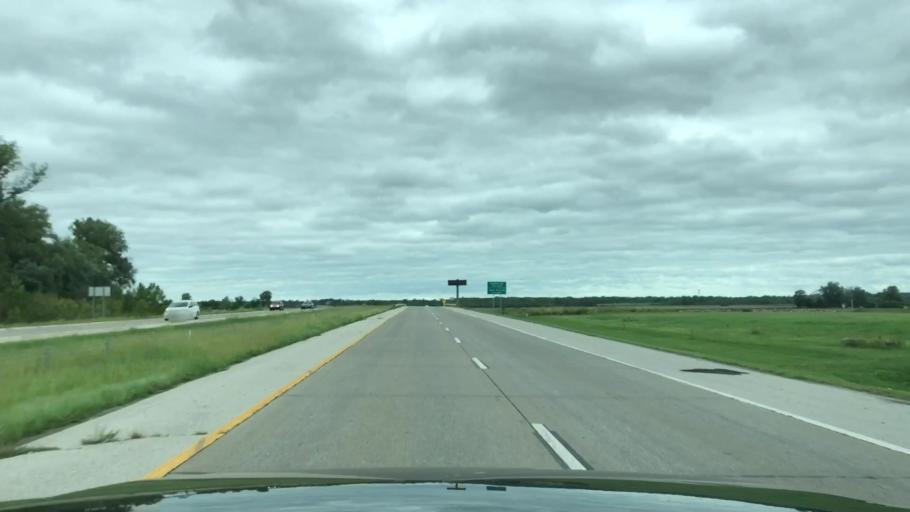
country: US
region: Missouri
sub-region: Saint Charles County
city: Saint Charles
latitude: 38.7297
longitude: -90.4892
